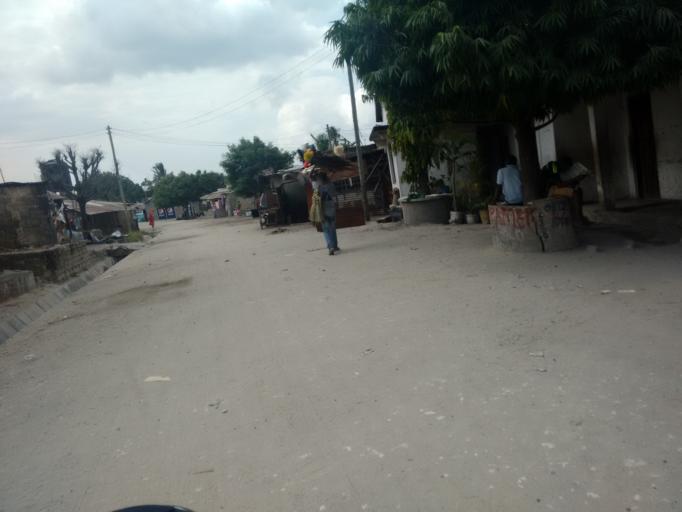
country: TZ
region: Dar es Salaam
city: Dar es Salaam
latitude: -6.8599
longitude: 39.2518
